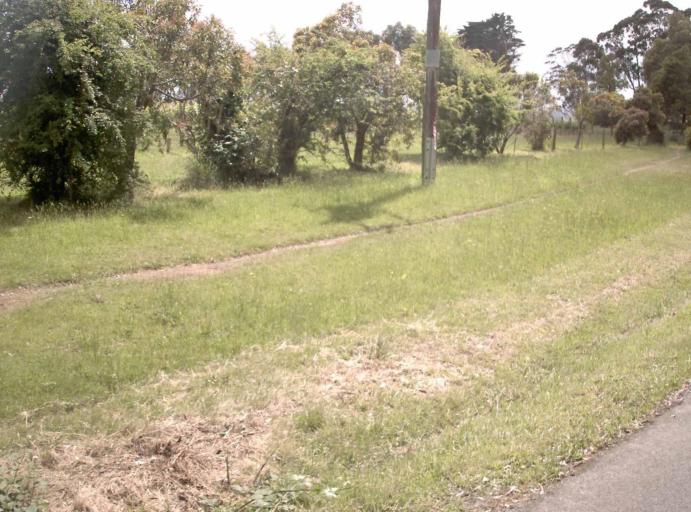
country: AU
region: Victoria
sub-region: Mornington Peninsula
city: Dromana
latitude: -38.3632
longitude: 144.9775
